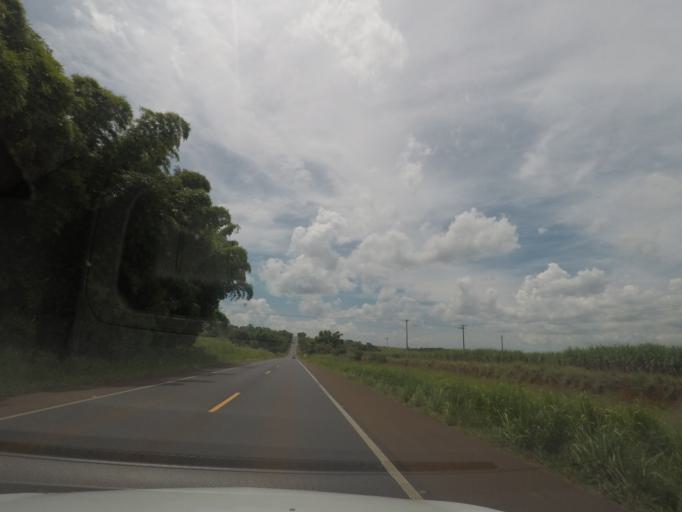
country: BR
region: Sao Paulo
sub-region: Barretos
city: Barretos
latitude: -20.4064
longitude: -48.6350
